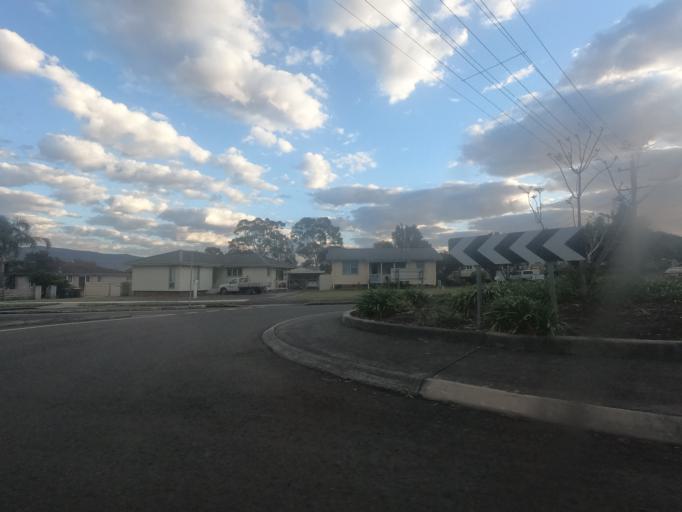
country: AU
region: New South Wales
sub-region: Wollongong
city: Koonawarra
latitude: -34.5032
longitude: 150.8038
